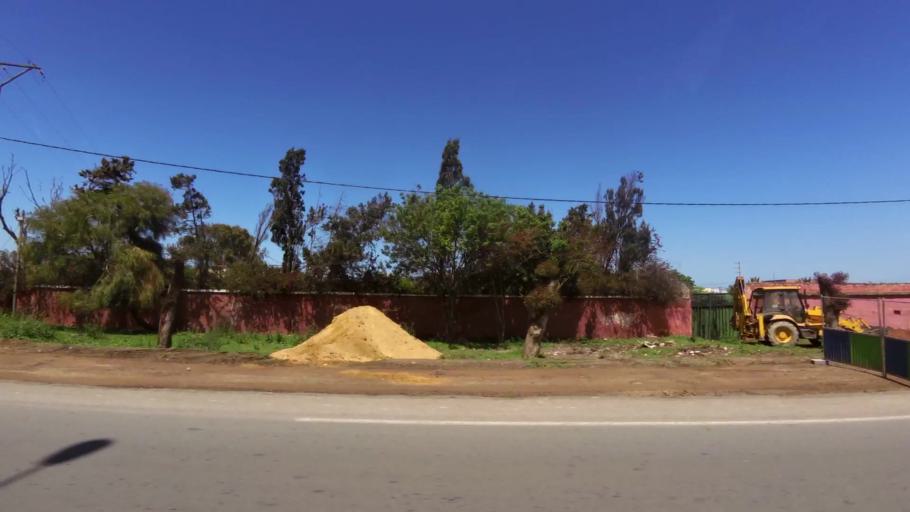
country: MA
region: Grand Casablanca
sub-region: Nouaceur
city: Dar Bouazza
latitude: 33.5177
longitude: -7.8007
